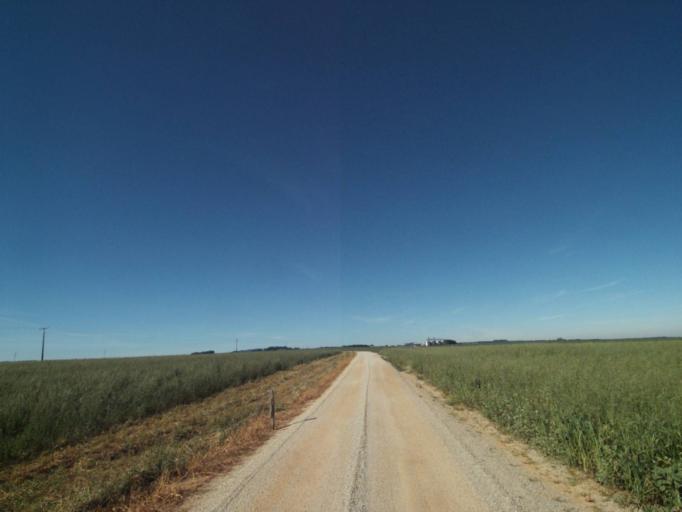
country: BR
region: Parana
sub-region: Tibagi
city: Tibagi
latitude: -24.5303
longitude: -50.3088
